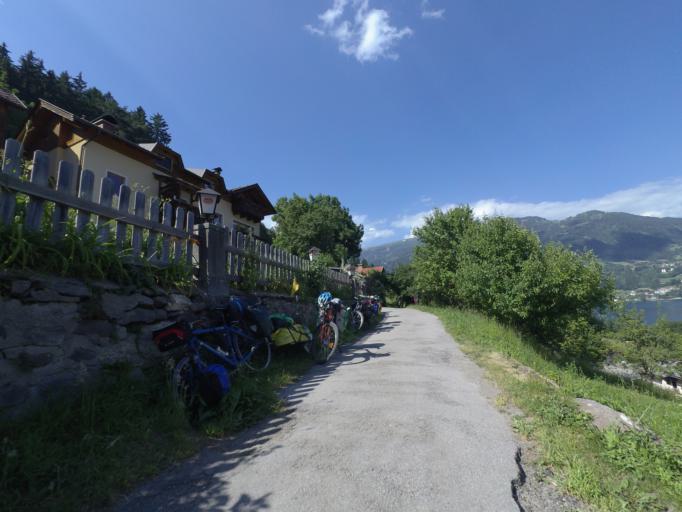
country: AT
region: Carinthia
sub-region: Politischer Bezirk Spittal an der Drau
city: Millstatt
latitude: 46.7795
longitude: 13.5915
